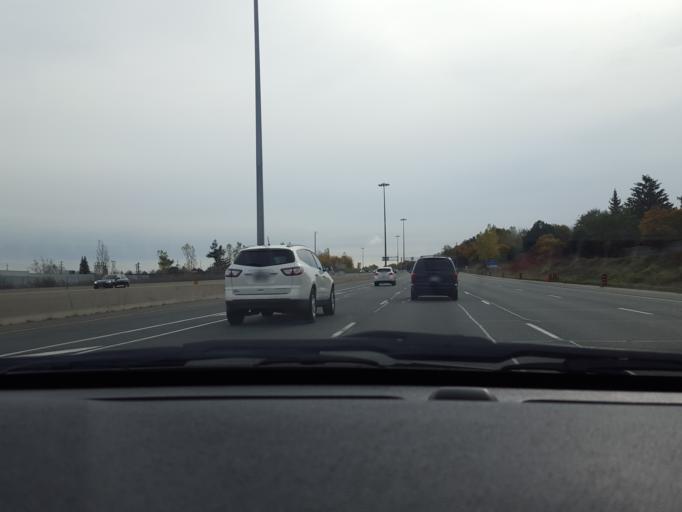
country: CA
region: Ontario
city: Willowdale
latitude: 43.8226
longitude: -79.3619
